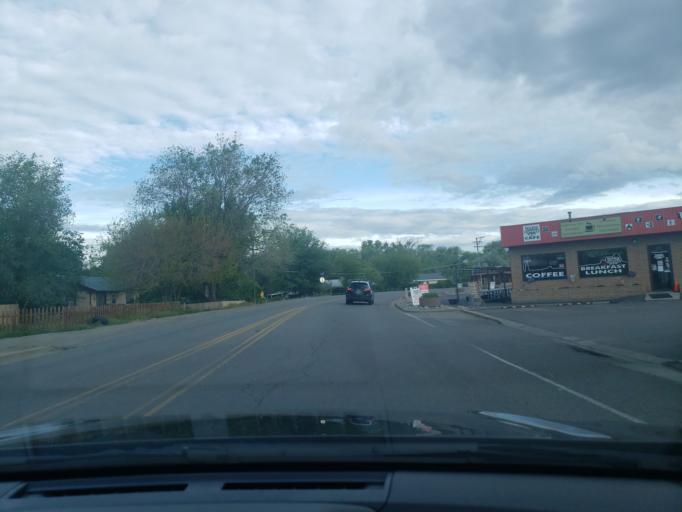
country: US
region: Colorado
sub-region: Mesa County
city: Grand Junction
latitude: 39.0654
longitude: -108.5857
